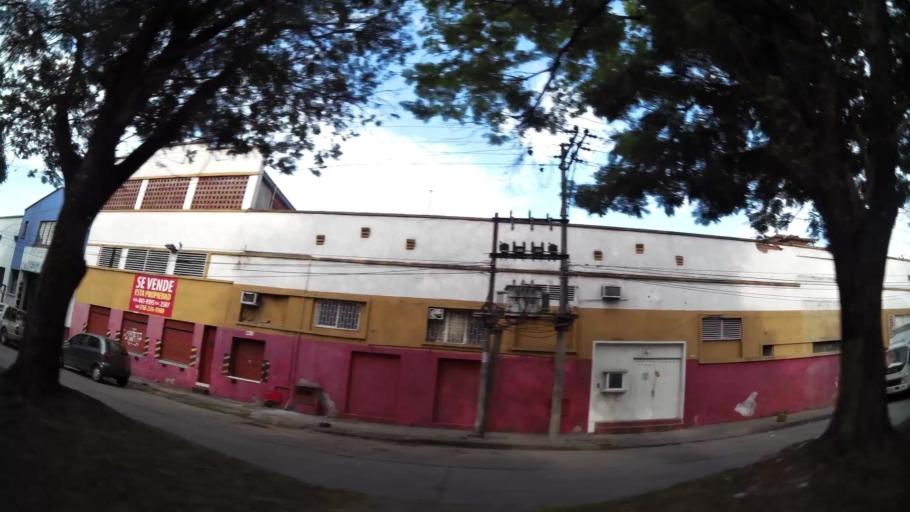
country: CO
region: Valle del Cauca
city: Cali
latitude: 3.4652
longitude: -76.5115
